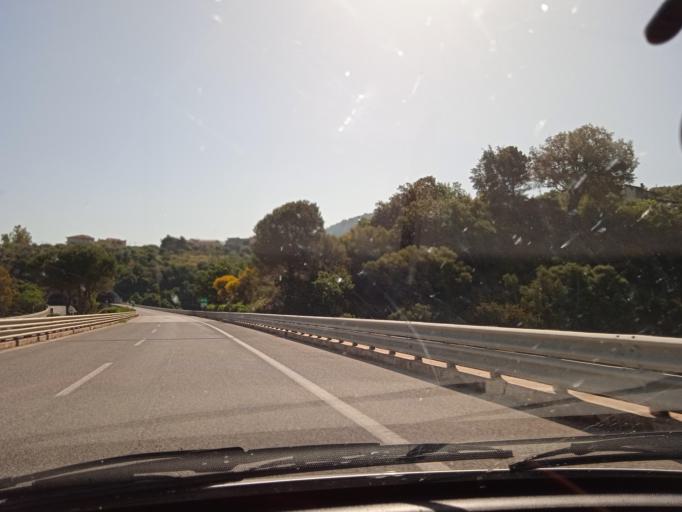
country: IT
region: Sicily
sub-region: Messina
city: Sant'Agata di Militello
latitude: 38.0631
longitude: 14.6431
